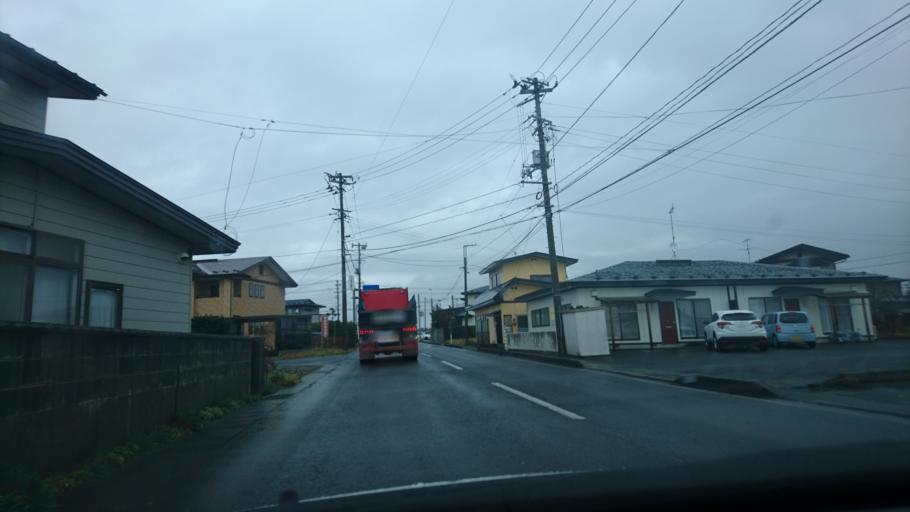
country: JP
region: Iwate
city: Kitakami
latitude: 39.2969
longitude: 141.0545
